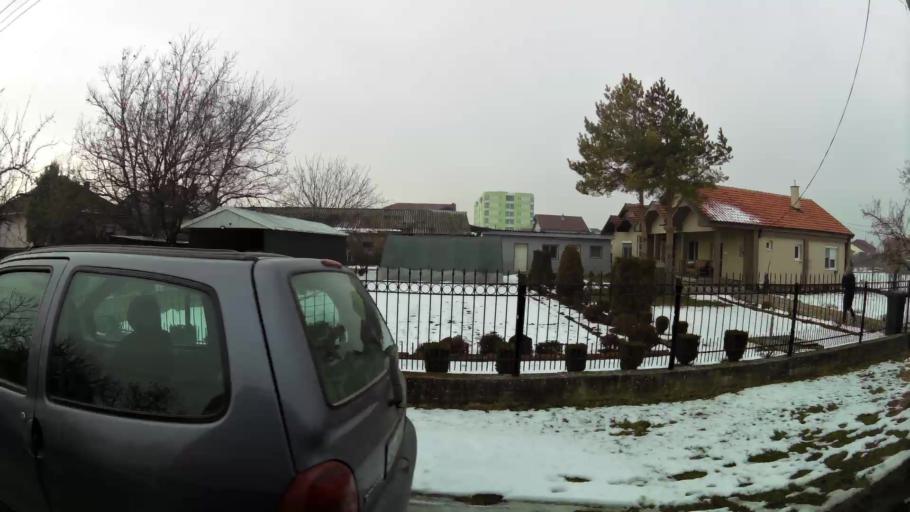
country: MK
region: Ilinden
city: Ilinden
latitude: 41.9965
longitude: 21.5824
